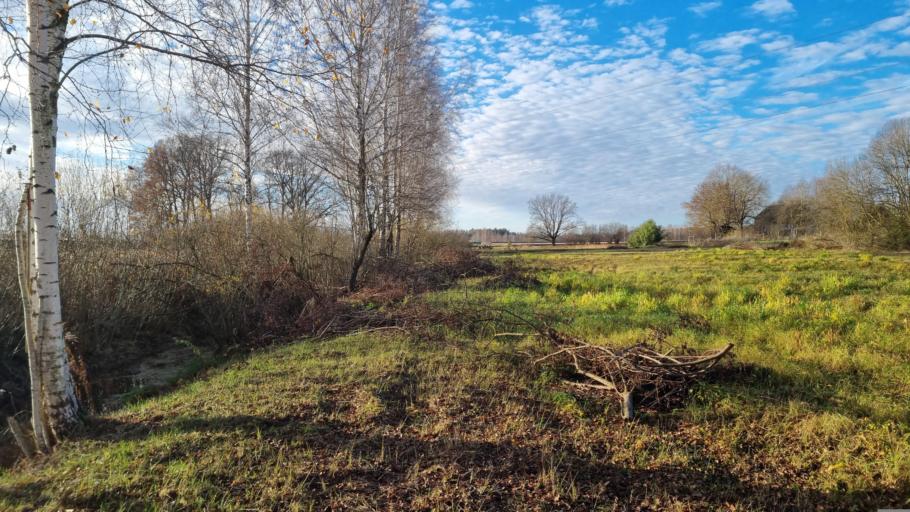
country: LV
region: Kekava
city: Kekava
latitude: 56.8135
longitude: 24.1959
